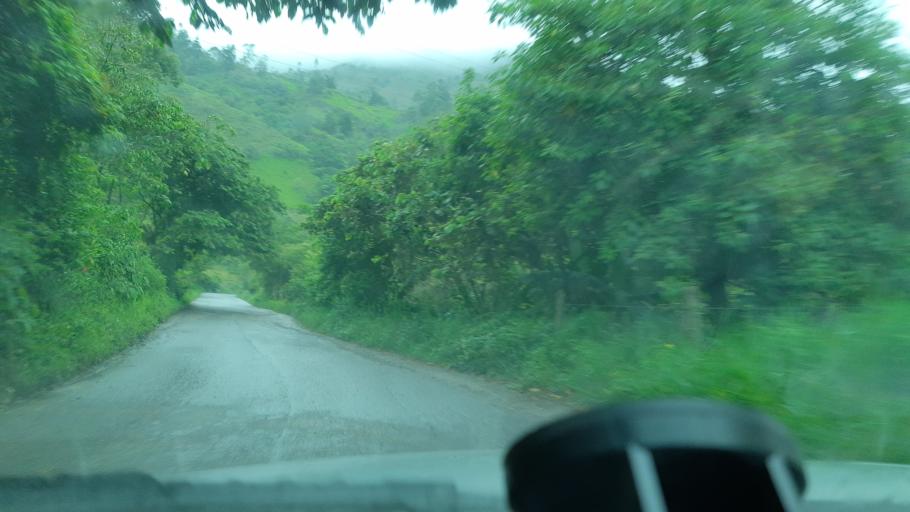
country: CO
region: Boyaca
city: Chinavita
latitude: 5.2067
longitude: -73.3887
